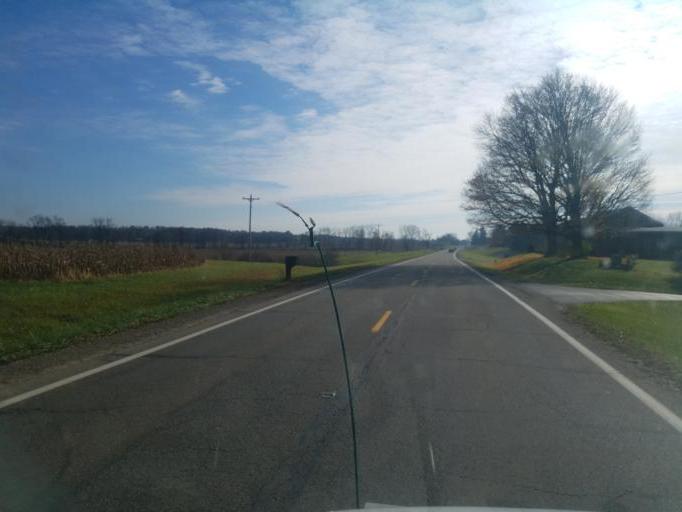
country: US
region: Ohio
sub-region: Knox County
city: Fredericktown
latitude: 40.4748
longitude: -82.6683
